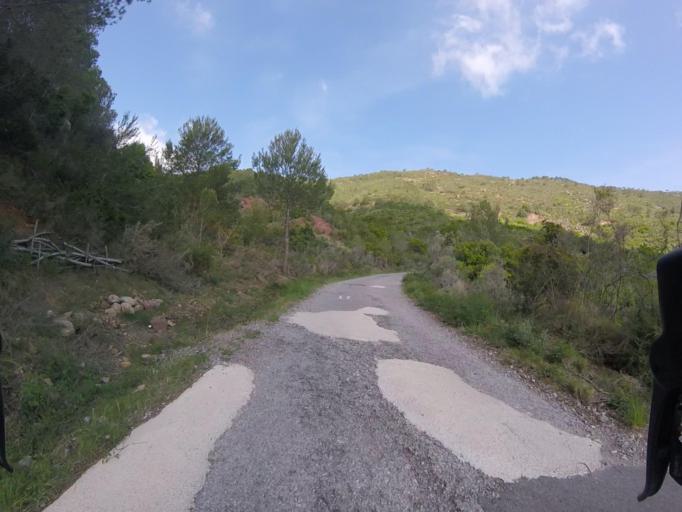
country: ES
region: Valencia
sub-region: Provincia de Castello
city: Benicassim
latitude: 40.0760
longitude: 0.0259
